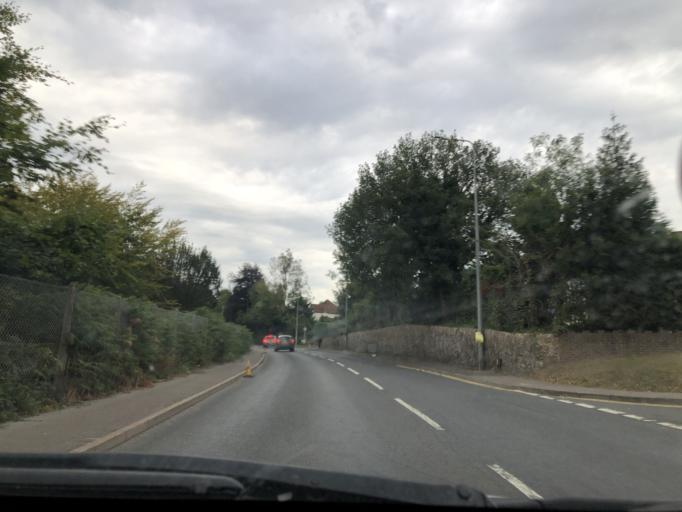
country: GB
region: England
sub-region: Kent
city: Sevenoaks
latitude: 51.2597
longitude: 0.1964
